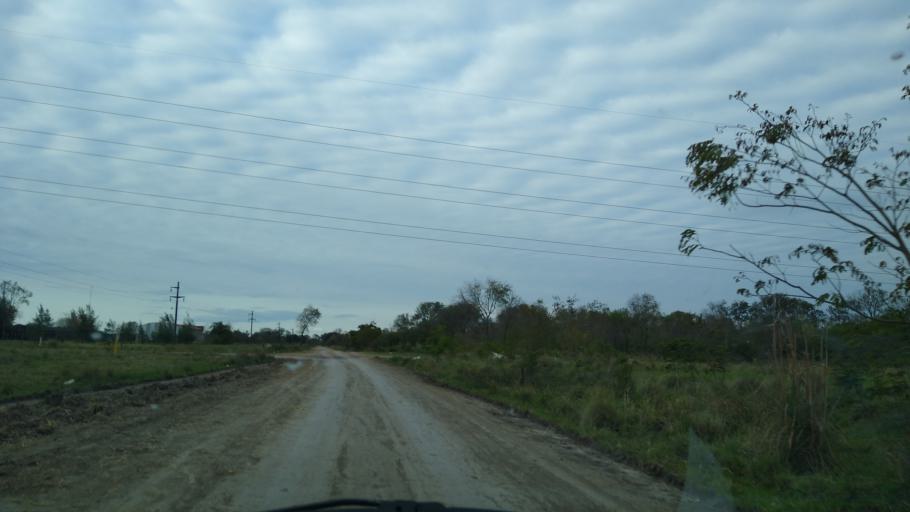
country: AR
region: Chaco
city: Fontana
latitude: -27.3870
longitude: -59.0458
